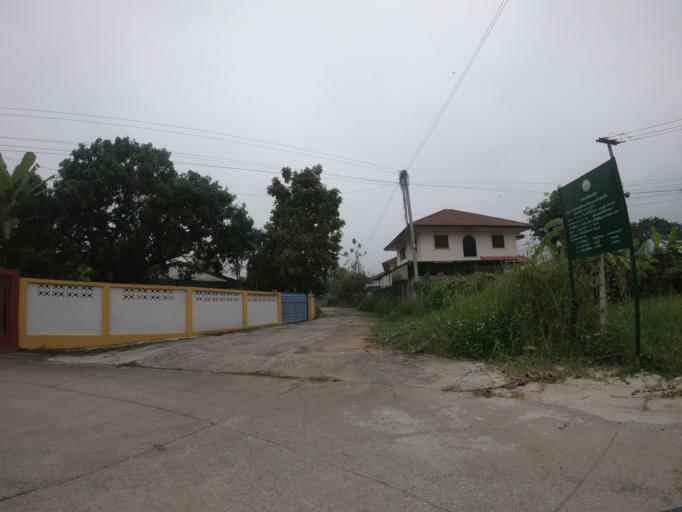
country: TH
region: Chiang Mai
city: Hang Dong
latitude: 18.7376
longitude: 98.9512
